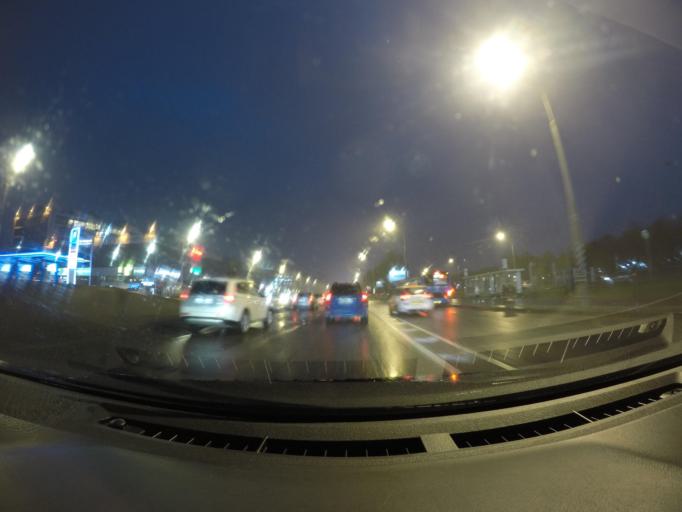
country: RU
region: Moskovskaya
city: Kozhukhovo
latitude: 55.6947
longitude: 37.6665
